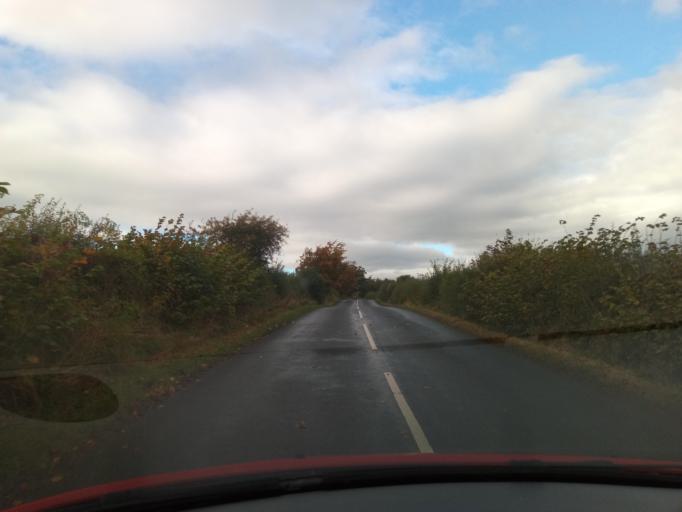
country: GB
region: Scotland
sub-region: The Scottish Borders
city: Newtown St Boswells
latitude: 55.5547
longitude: -2.7070
